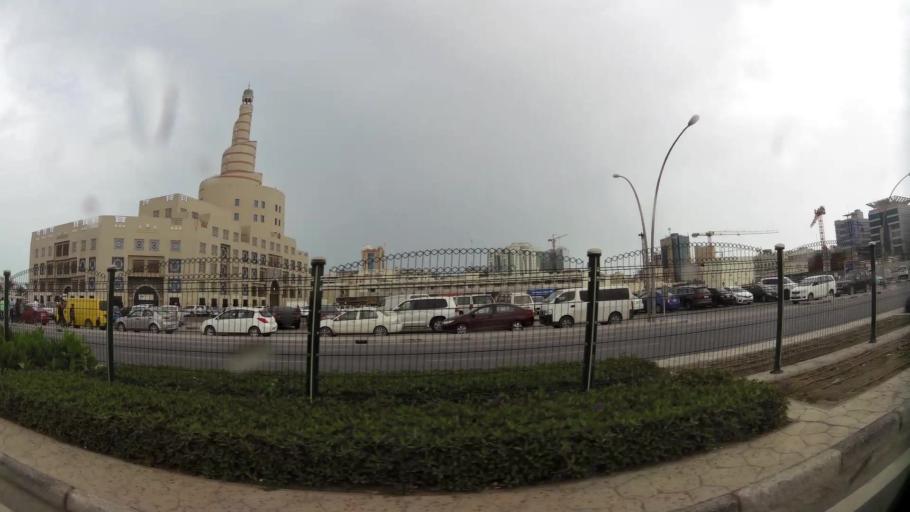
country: QA
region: Baladiyat ad Dawhah
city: Doha
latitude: 25.2881
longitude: 51.5346
